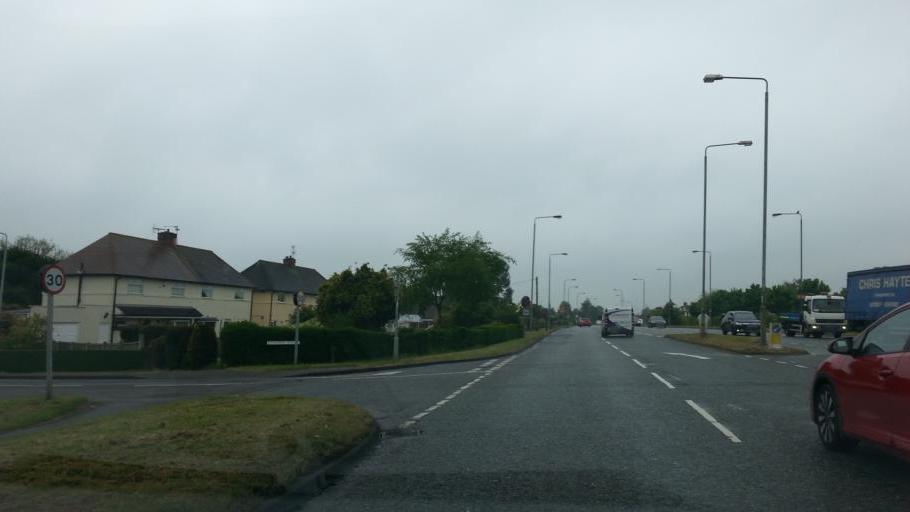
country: GB
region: England
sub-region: Nottinghamshire
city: Newark on Trent
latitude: 53.0911
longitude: -0.7903
